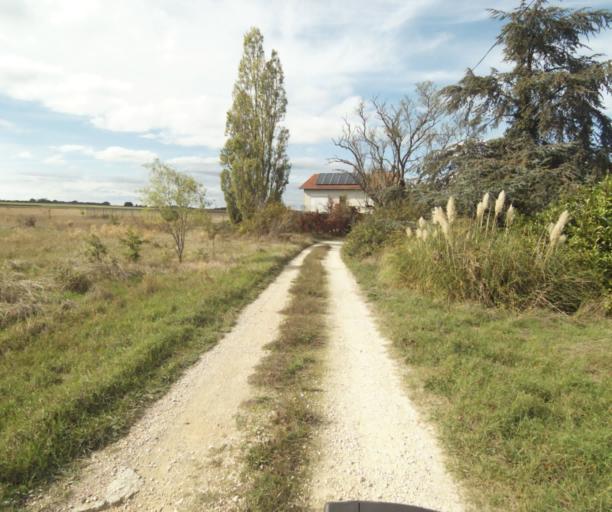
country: FR
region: Midi-Pyrenees
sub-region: Departement du Tarn-et-Garonne
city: Saint-Porquier
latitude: 43.9435
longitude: 1.1350
